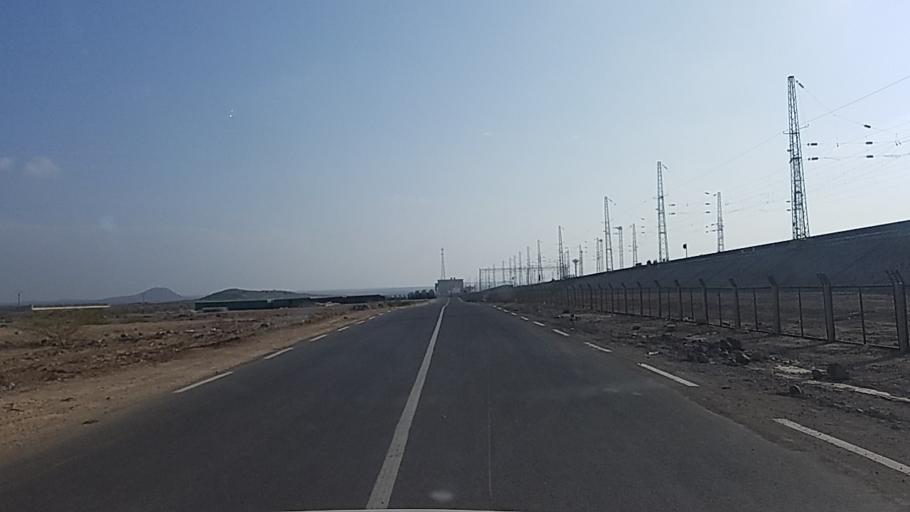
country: DJ
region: Djibouti
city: Djibouti
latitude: 11.5298
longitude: 43.1333
